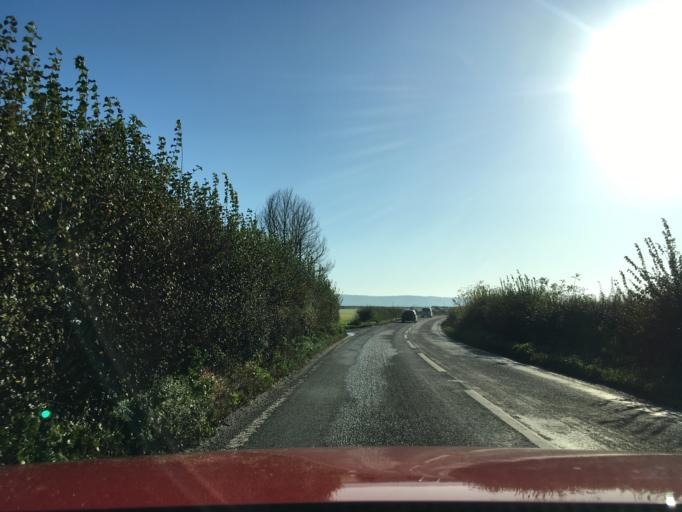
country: GB
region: England
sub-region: Somerset
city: Westonzoyland
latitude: 51.0915
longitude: -2.8831
